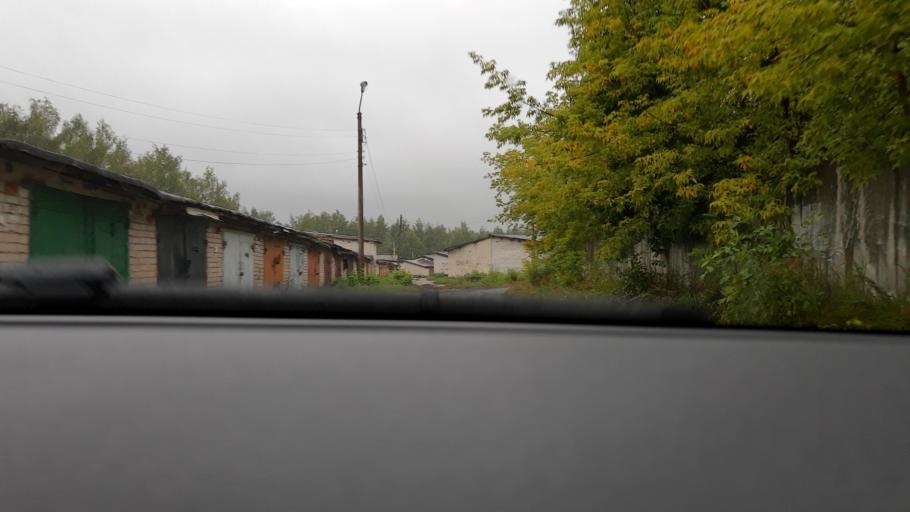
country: RU
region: Nizjnij Novgorod
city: Gorbatovka
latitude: 56.3274
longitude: 43.8356
